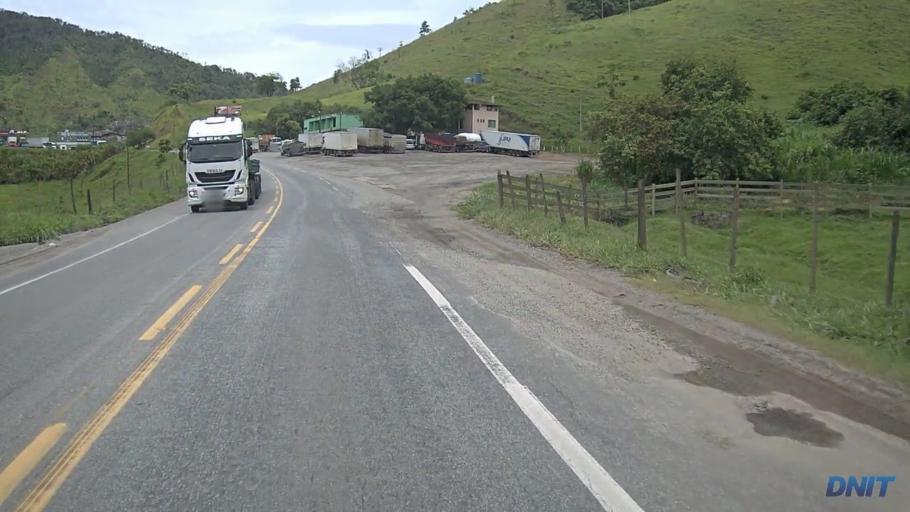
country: BR
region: Minas Gerais
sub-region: Timoteo
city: Timoteo
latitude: -19.6204
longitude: -42.8423
